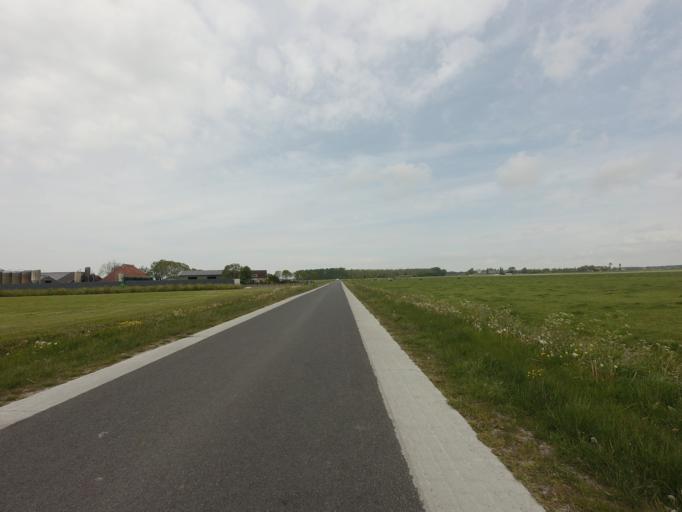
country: NL
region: Friesland
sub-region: Sudwest Fryslan
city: Bolsward
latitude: 53.0891
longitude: 5.4817
